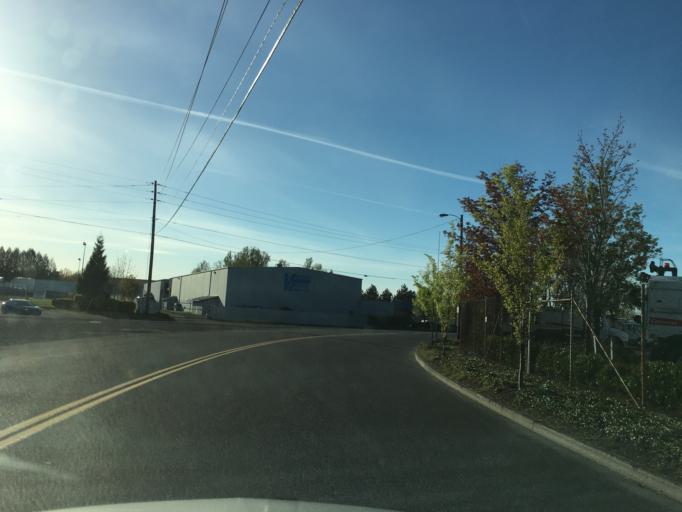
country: US
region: Oregon
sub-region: Multnomah County
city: Lents
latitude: 45.5583
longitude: -122.5282
